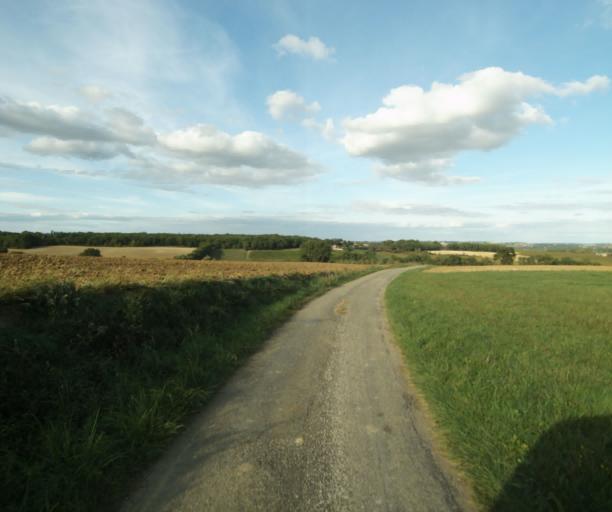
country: FR
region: Midi-Pyrenees
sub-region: Departement du Gers
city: Gondrin
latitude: 43.8959
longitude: 0.2685
